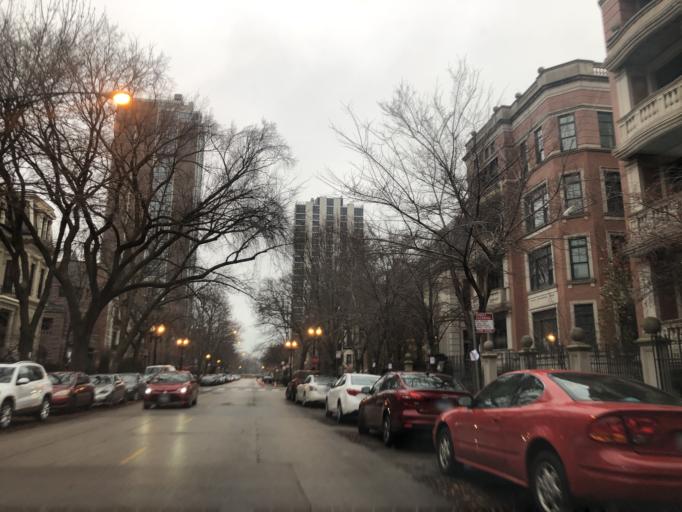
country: US
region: Illinois
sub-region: Cook County
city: Chicago
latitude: 41.9087
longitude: -87.6301
